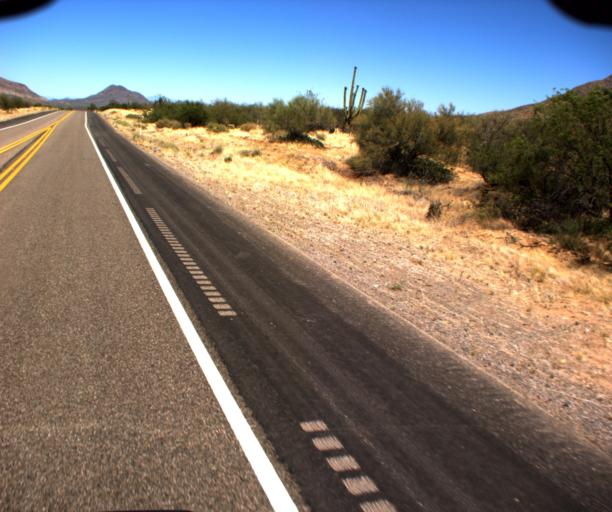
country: US
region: Arizona
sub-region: Pima County
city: Three Points
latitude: 32.0322
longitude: -111.5553
